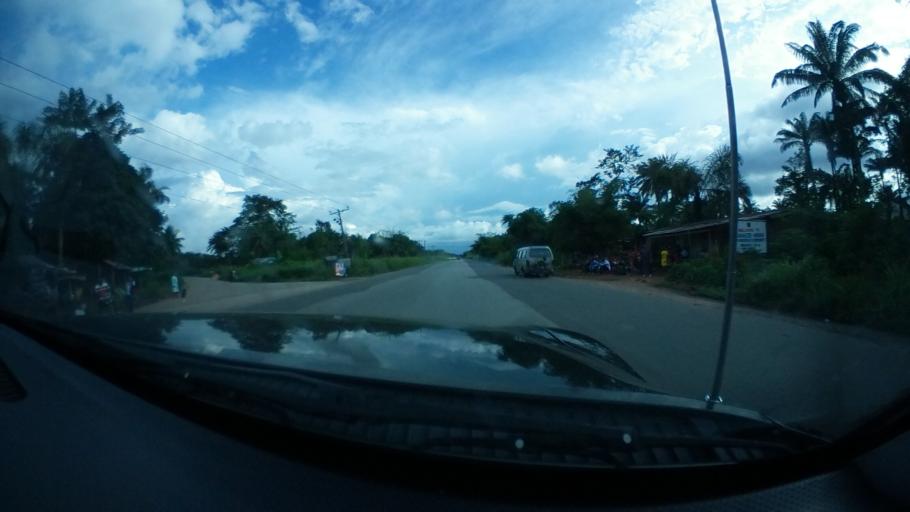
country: NG
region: Imo
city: Orodo
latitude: 5.6350
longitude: 7.0227
